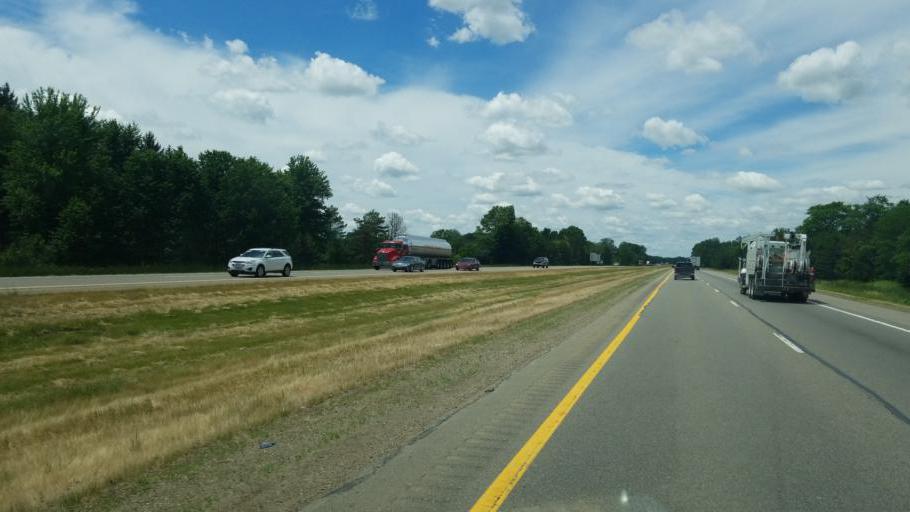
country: US
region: Michigan
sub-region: Eaton County
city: Dimondale
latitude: 42.6658
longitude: -84.6111
